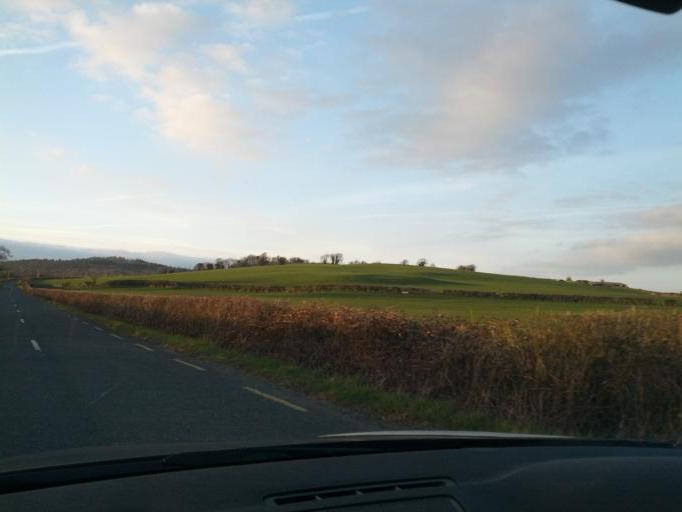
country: IE
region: Munster
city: Nenagh Bridge
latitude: 52.9583
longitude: -8.2362
